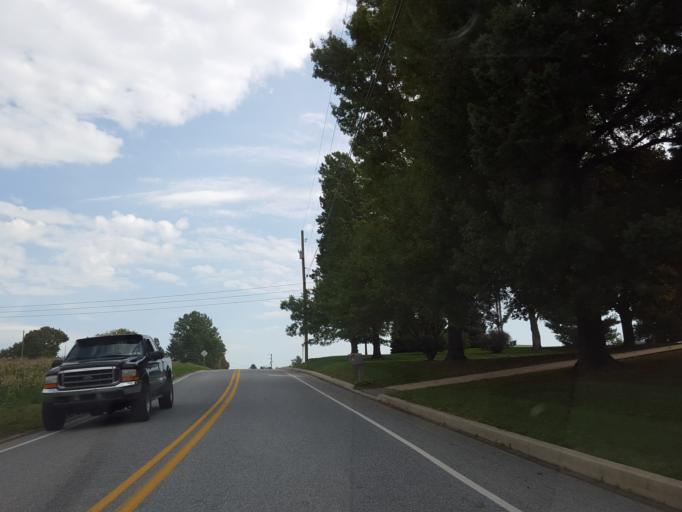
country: US
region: Pennsylvania
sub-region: York County
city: Spry
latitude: 39.9162
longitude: -76.6744
